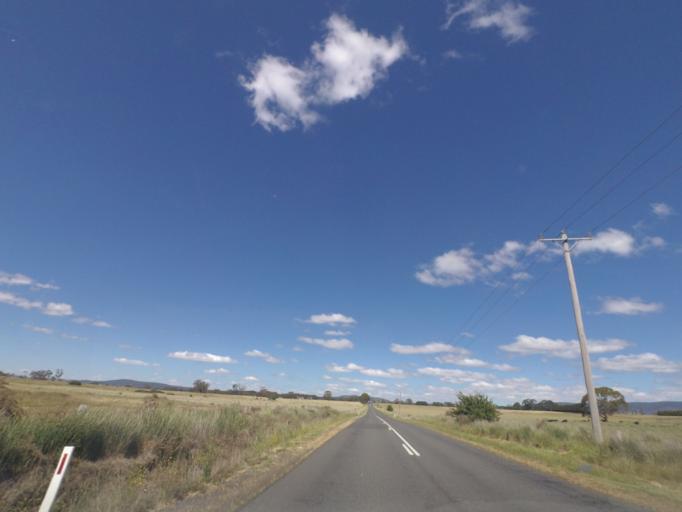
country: AU
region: Victoria
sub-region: Mount Alexander
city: Castlemaine
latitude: -37.2900
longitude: 144.4782
